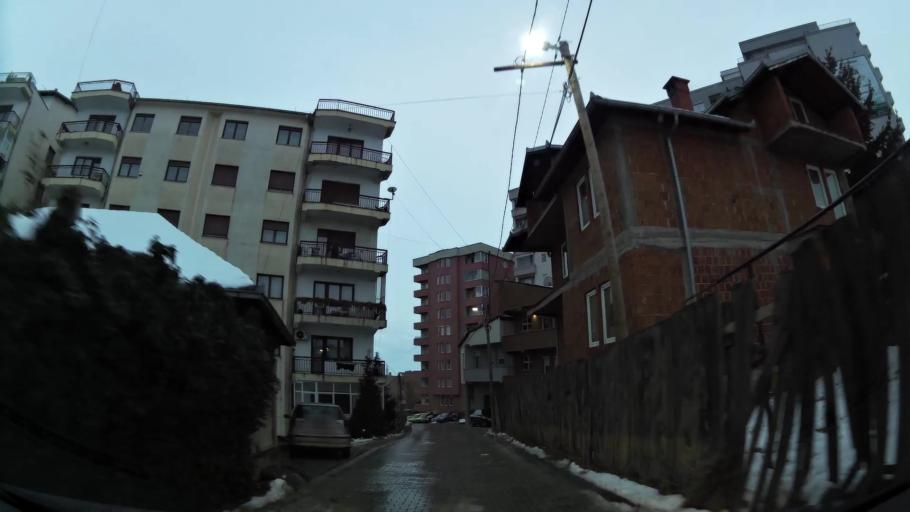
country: XK
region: Pristina
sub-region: Komuna e Prishtines
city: Pristina
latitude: 42.6585
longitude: 21.1778
